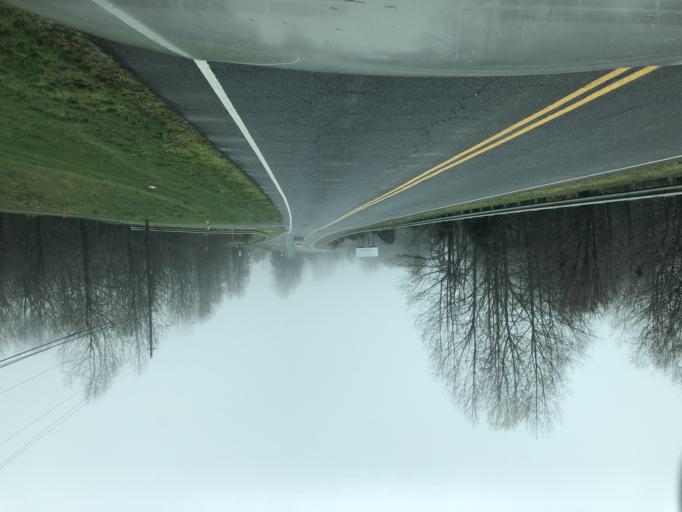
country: US
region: North Carolina
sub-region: Gaston County
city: Cherryville
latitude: 35.3595
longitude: -81.4338
